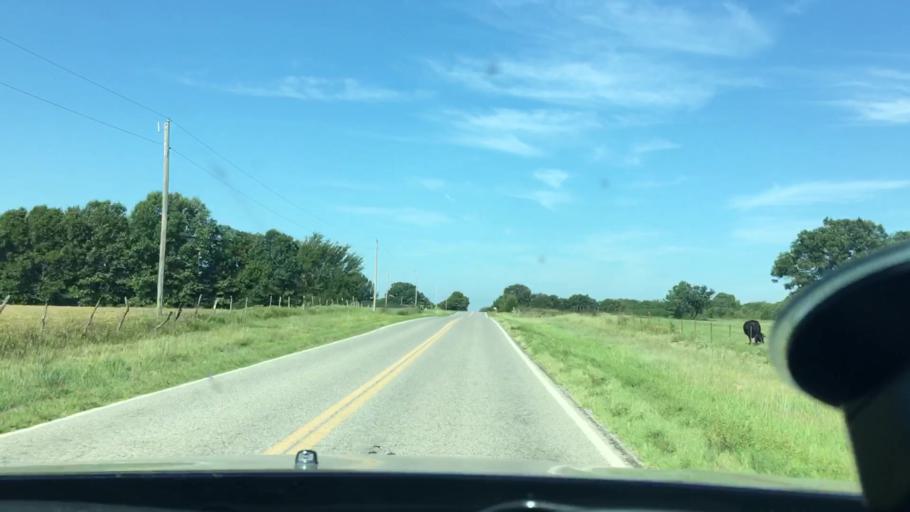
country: US
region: Oklahoma
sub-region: Johnston County
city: Tishomingo
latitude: 34.2742
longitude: -96.5240
